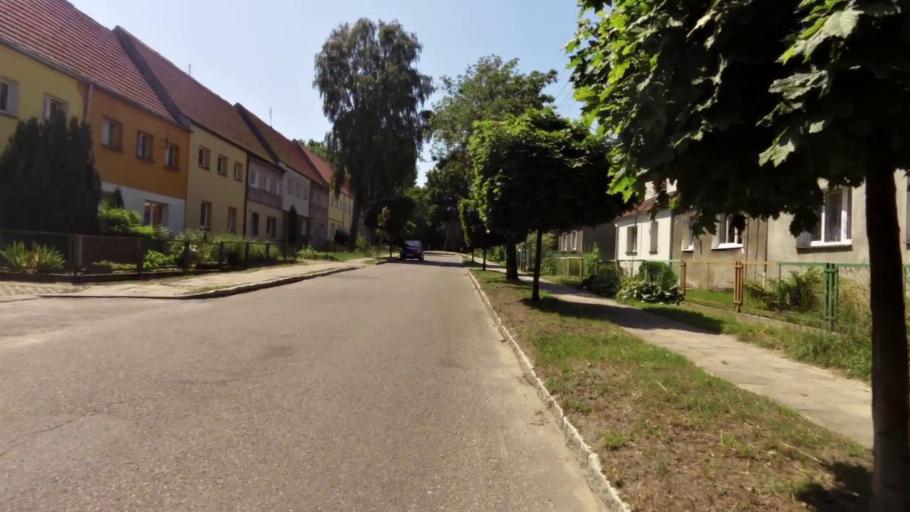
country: PL
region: West Pomeranian Voivodeship
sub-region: Powiat swidwinski
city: Polczyn-Zdroj
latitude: 53.7713
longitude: 16.1033
